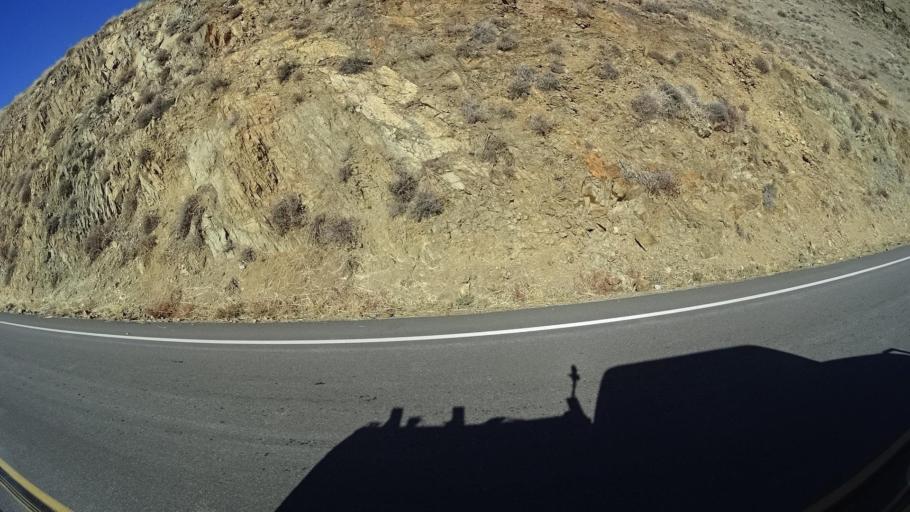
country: US
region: California
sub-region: Kern County
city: Wofford Heights
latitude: 35.6849
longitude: -118.4256
